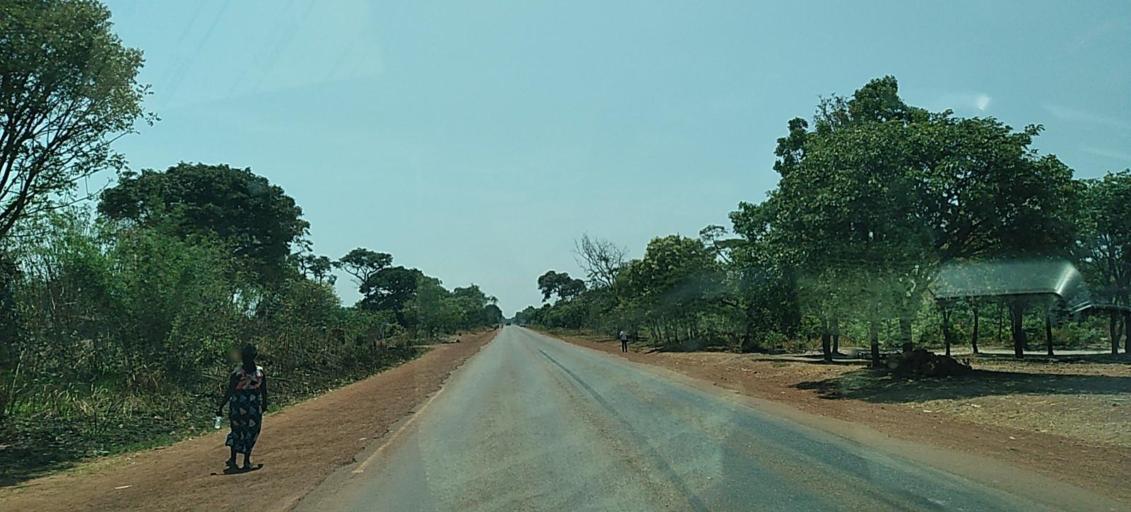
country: ZM
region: North-Western
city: Solwezi
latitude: -12.3614
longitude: 25.9423
